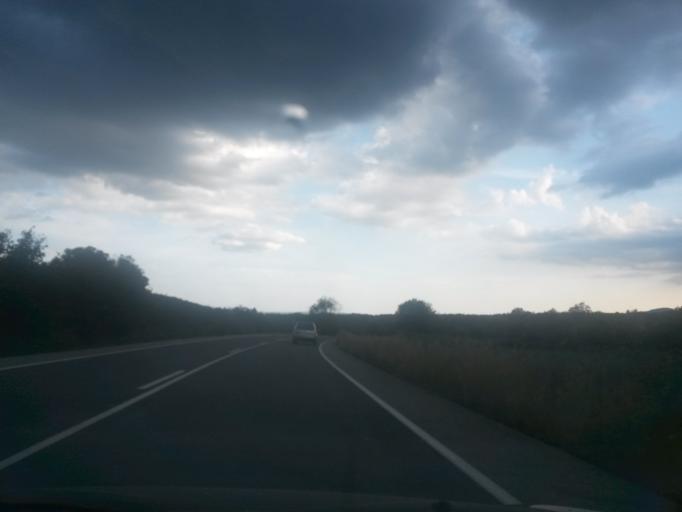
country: ES
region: Catalonia
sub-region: Provincia de Girona
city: Brunyola
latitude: 41.9130
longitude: 2.6590
